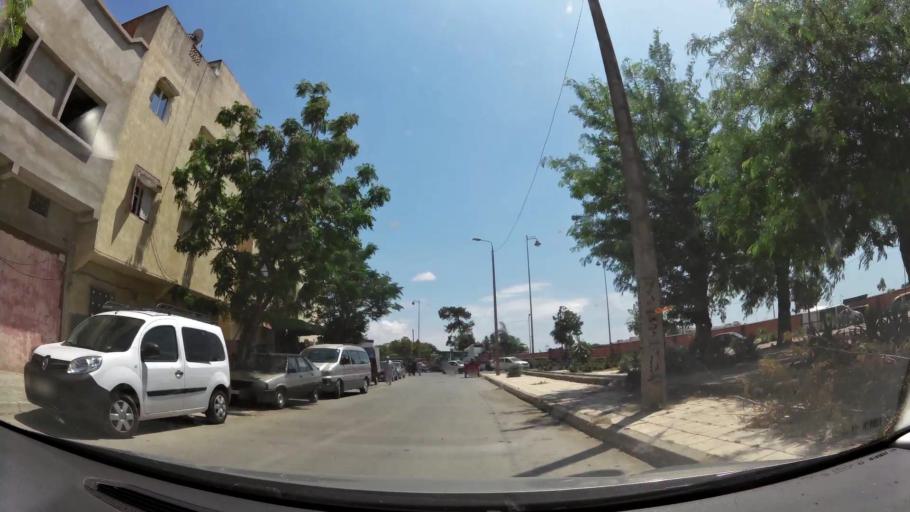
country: MA
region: Gharb-Chrarda-Beni Hssen
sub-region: Kenitra Province
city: Kenitra
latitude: 34.2549
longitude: -6.5597
